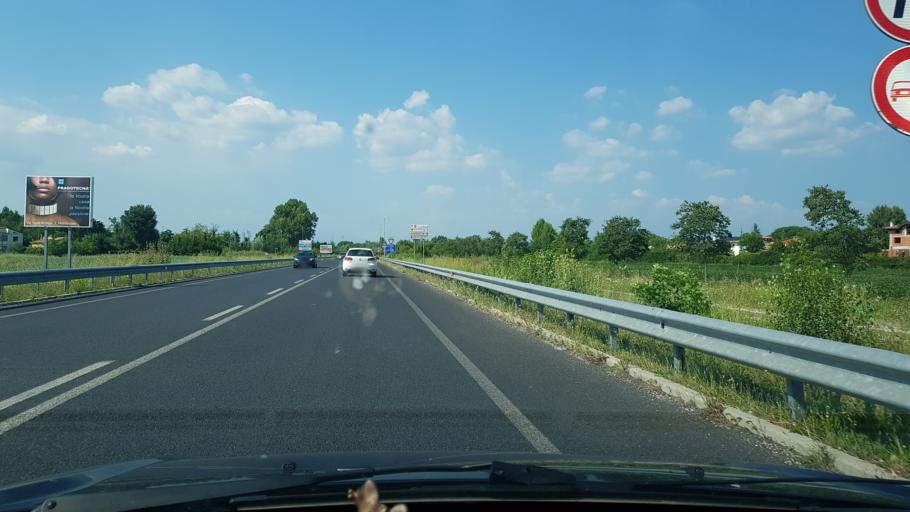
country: IT
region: Friuli Venezia Giulia
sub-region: Provincia di Gorizia
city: Staranzano
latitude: 45.8029
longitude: 13.4882
